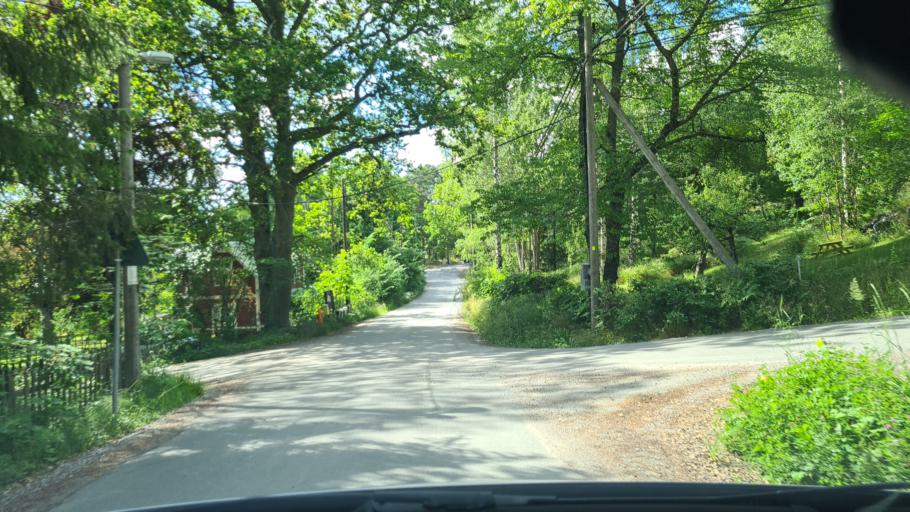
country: SE
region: Stockholm
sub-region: Vaxholms Kommun
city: Vaxholm
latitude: 59.4110
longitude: 18.3767
